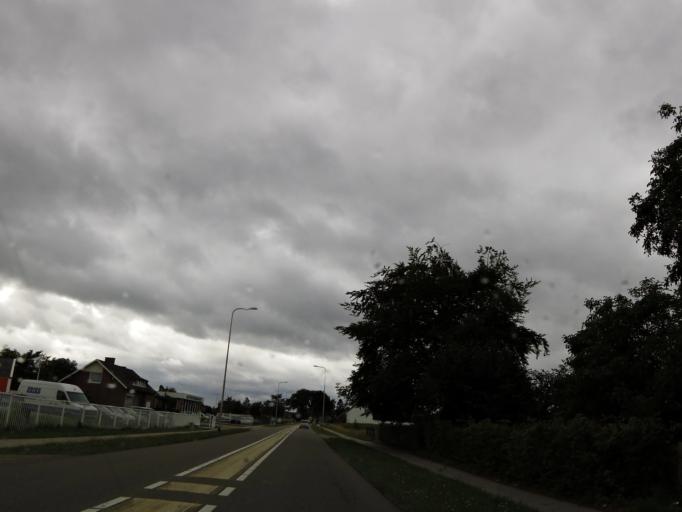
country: NL
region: Limburg
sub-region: Gemeente Maasgouw
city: Maasbracht
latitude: 51.0945
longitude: 5.8831
